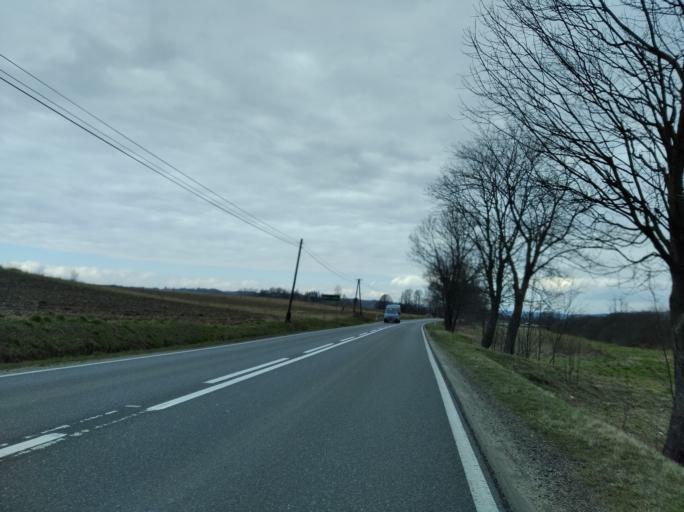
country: PL
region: Subcarpathian Voivodeship
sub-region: Powiat krosnienski
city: Wojaszowka
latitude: 49.7865
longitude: 21.6617
